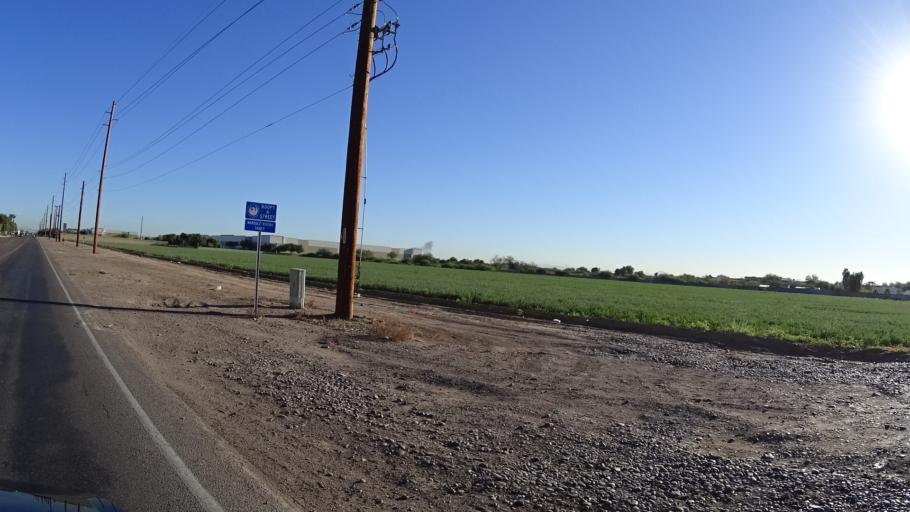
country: US
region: Arizona
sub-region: Maricopa County
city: Tolleson
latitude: 33.4234
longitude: -112.2211
